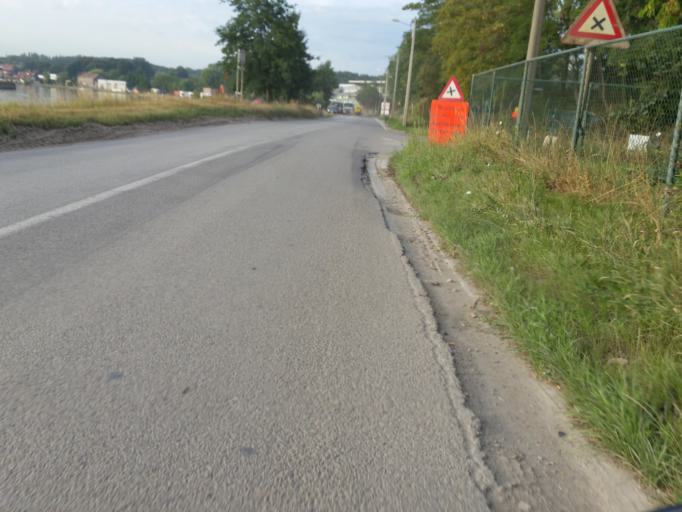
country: BE
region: Flanders
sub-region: Provincie Vlaams-Brabant
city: Vilvoorde
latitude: 50.9344
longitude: 4.4123
